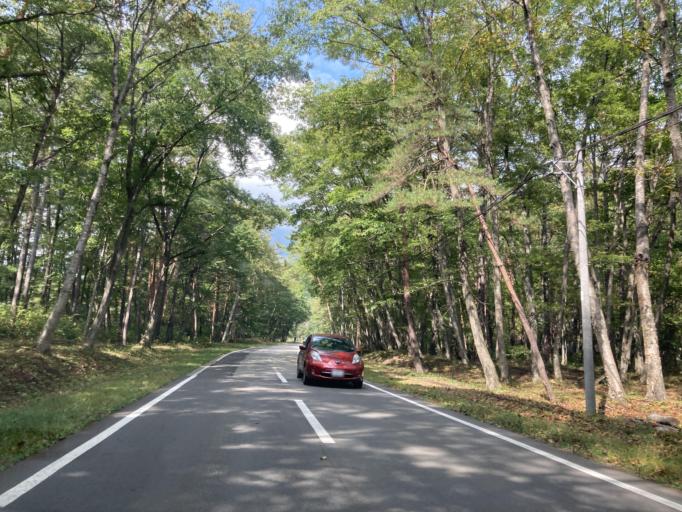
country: JP
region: Nagano
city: Omachi
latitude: 36.5313
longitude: 137.7946
